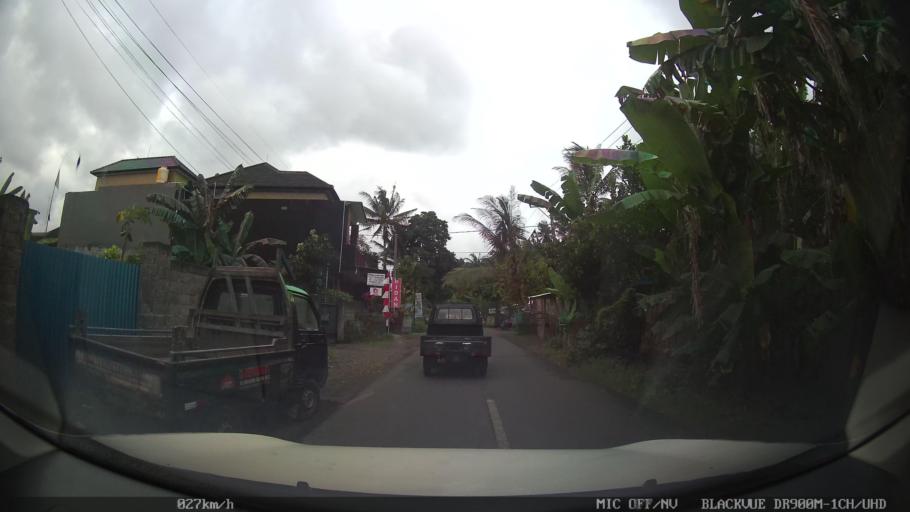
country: ID
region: Bali
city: Banjar Parekan
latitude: -8.5679
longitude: 115.2103
